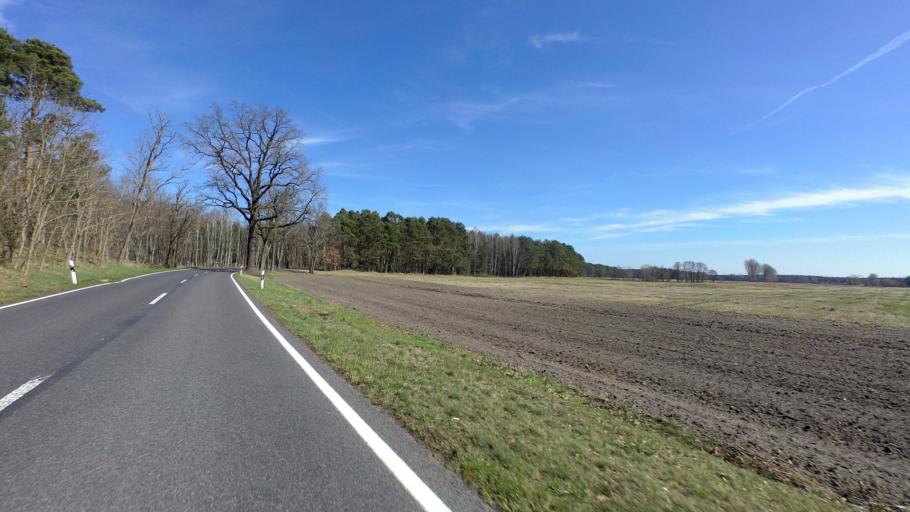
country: DE
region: Brandenburg
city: Munchehofe
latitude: 52.1243
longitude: 13.8013
